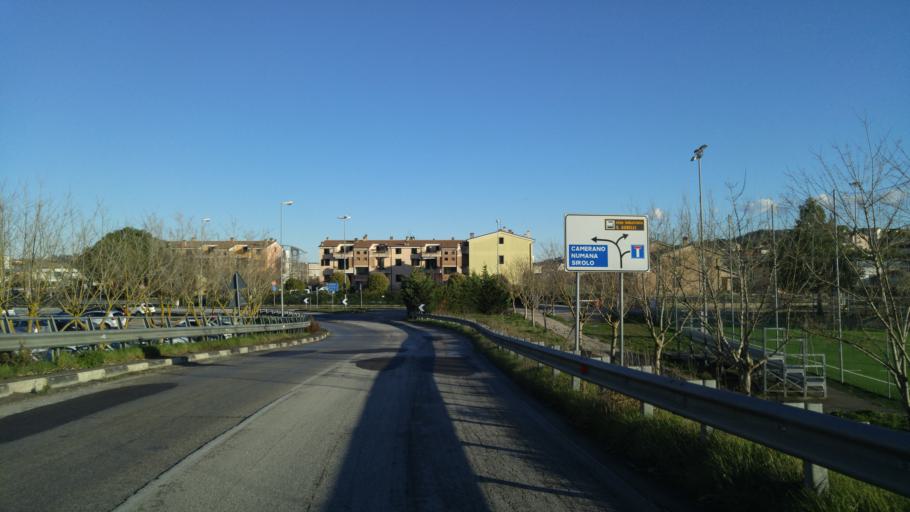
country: IT
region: The Marches
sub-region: Provincia di Ancona
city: Camerano
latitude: 43.4992
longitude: 13.5418
